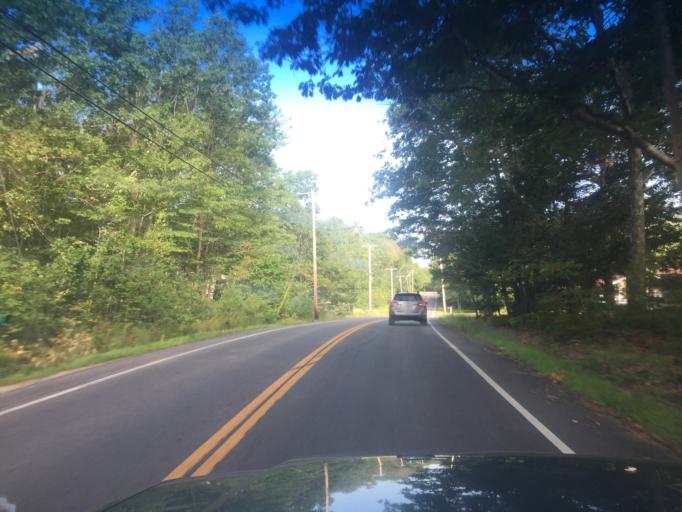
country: US
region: Maine
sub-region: York County
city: South Berwick
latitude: 43.2060
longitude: -70.7784
